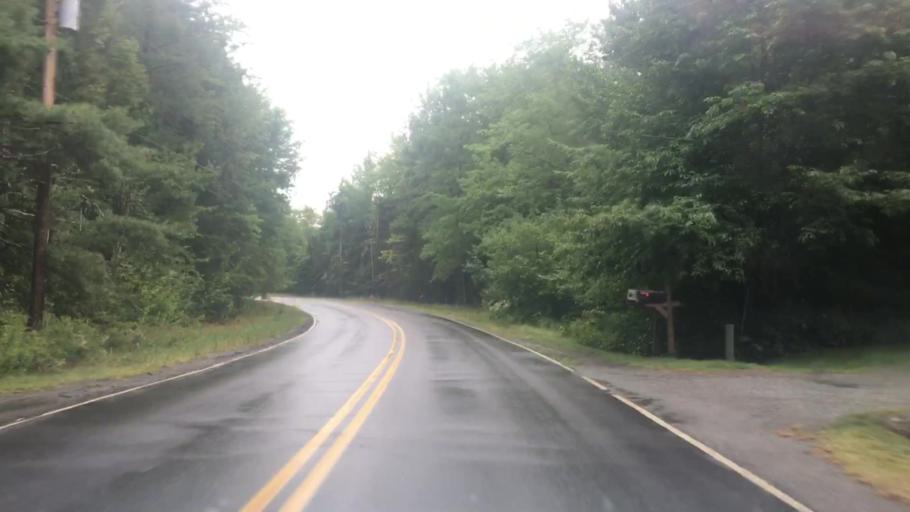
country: US
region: Maine
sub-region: Penobscot County
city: Hudson
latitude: 44.9873
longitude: -68.7968
